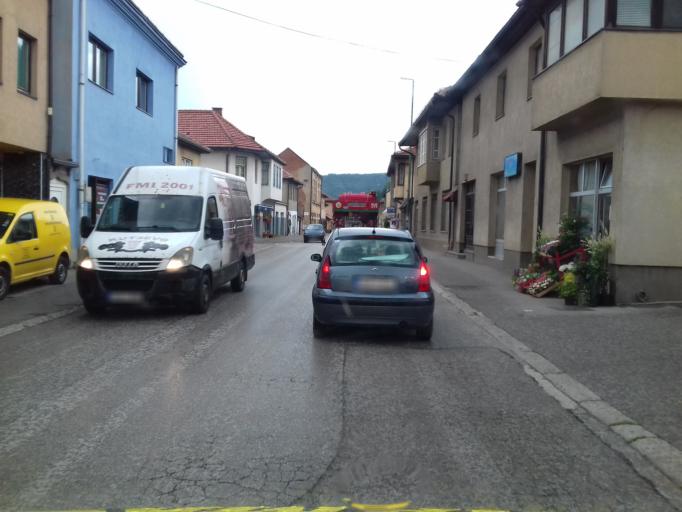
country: BA
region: Federation of Bosnia and Herzegovina
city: Visoko
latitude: 43.9866
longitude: 18.1786
